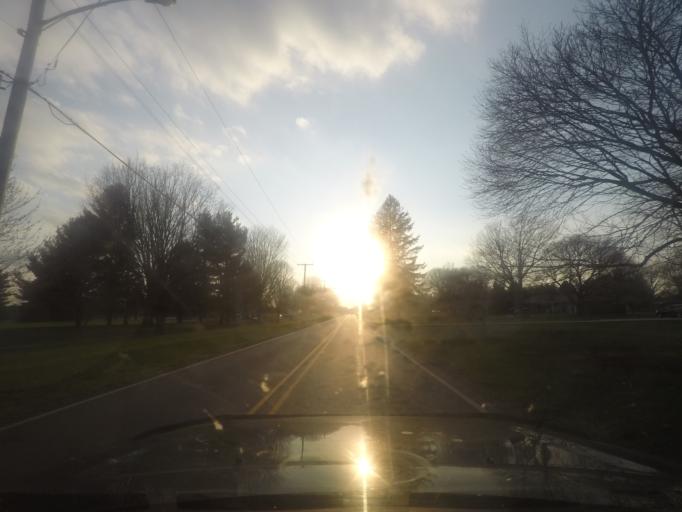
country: US
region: Indiana
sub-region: LaPorte County
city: LaPorte
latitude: 41.5915
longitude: -86.7129
